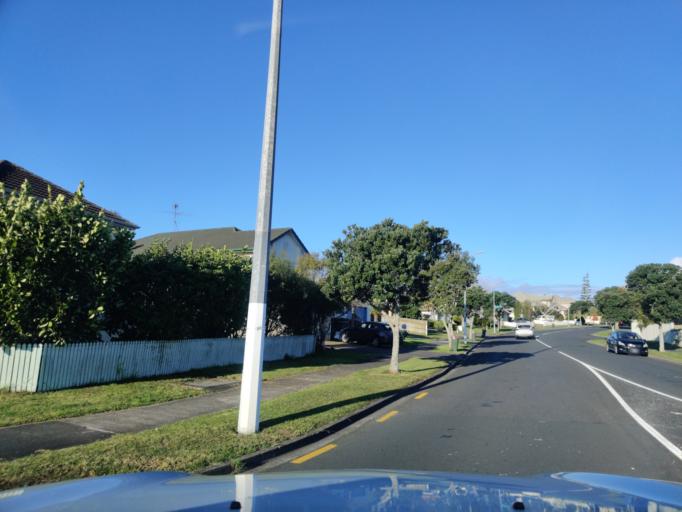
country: NZ
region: Auckland
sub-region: Auckland
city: Pakuranga
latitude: -36.9166
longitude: 174.9195
